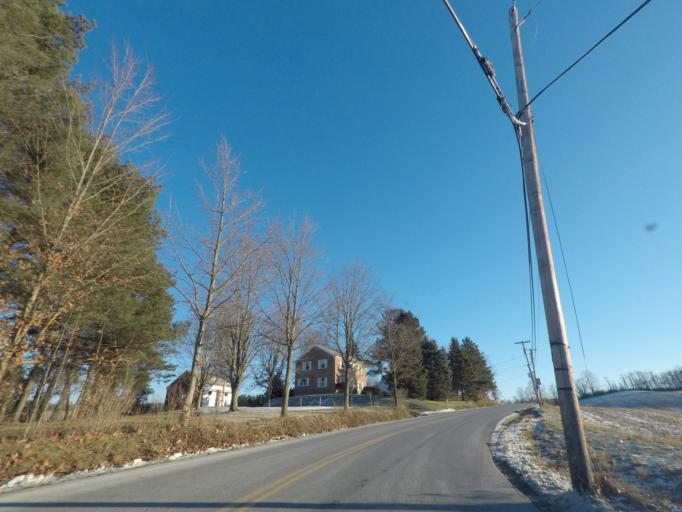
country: US
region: New York
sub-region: Rensselaer County
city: Poestenkill
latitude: 42.7277
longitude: -73.5971
